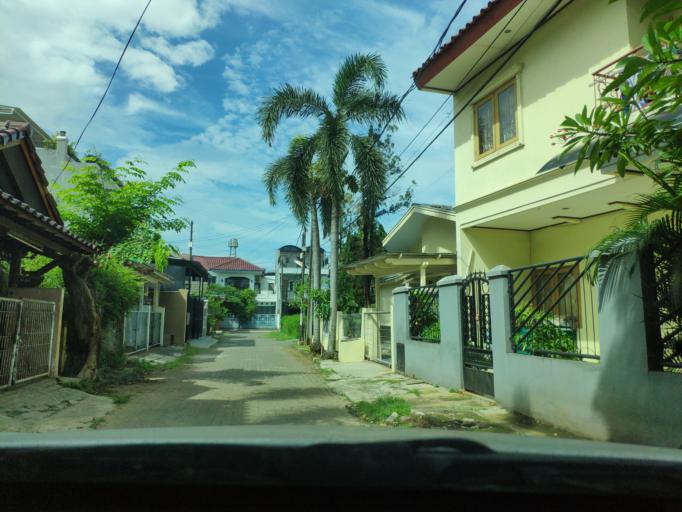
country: ID
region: West Java
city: Ciputat
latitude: -6.2242
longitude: 106.7098
